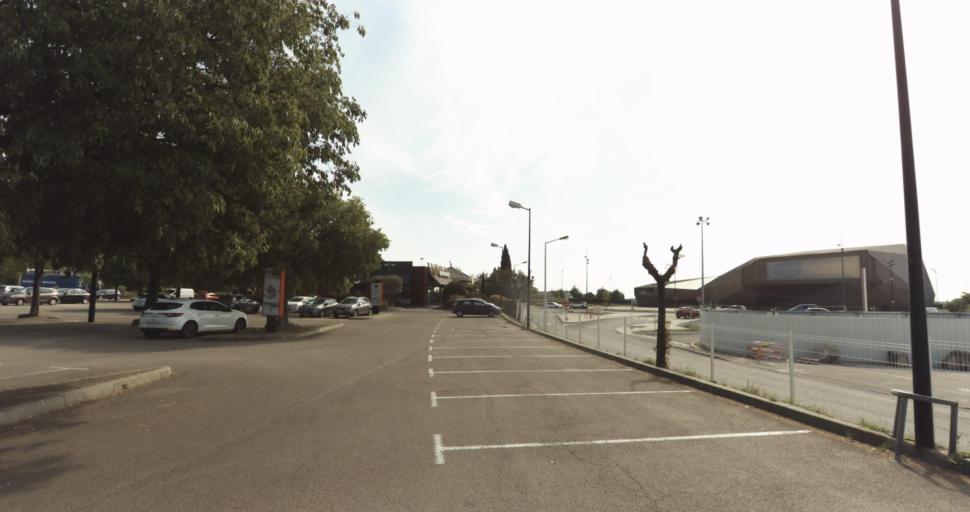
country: FR
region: Languedoc-Roussillon
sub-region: Departement du Gard
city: Rodilhan
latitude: 43.8566
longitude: 4.4030
